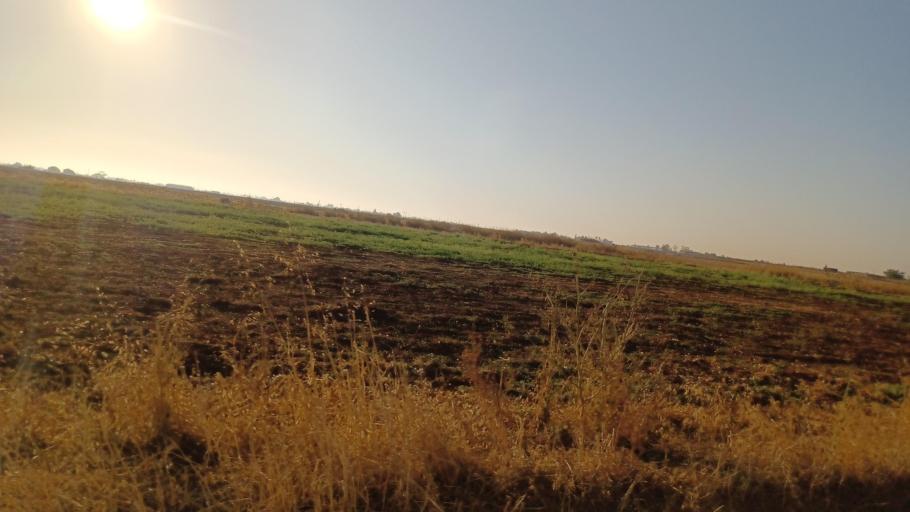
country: CY
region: Ammochostos
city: Achna
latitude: 35.0311
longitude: 33.7914
